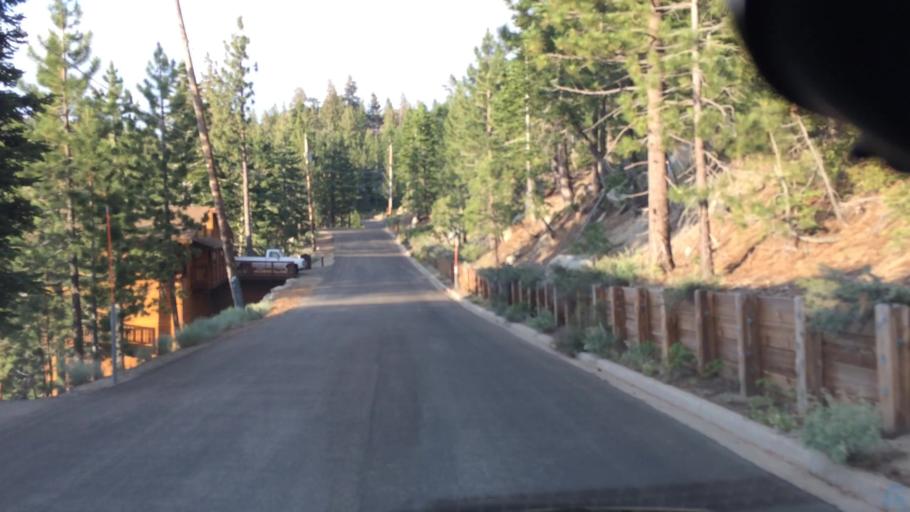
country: US
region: Nevada
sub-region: Douglas County
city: Kingsbury
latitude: 38.9701
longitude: -119.8919
